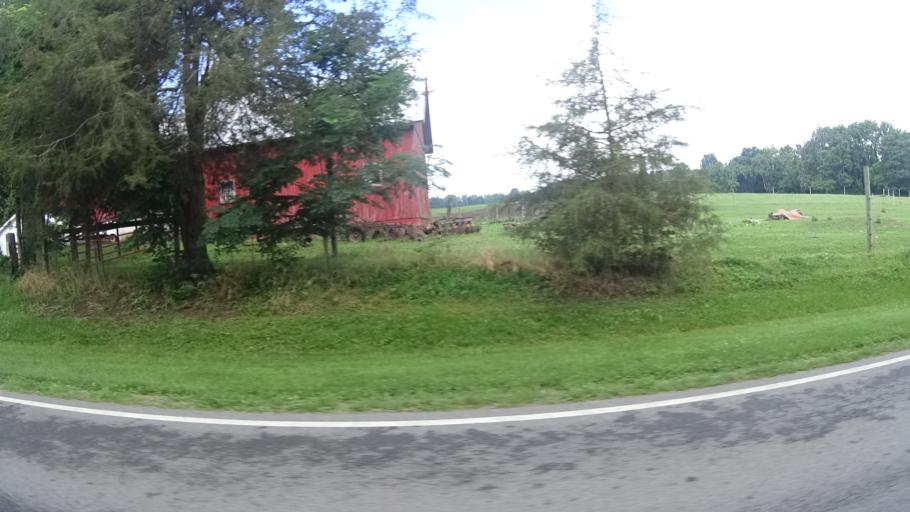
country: US
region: Ohio
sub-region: Huron County
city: Wakeman
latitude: 41.3085
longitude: -82.4134
